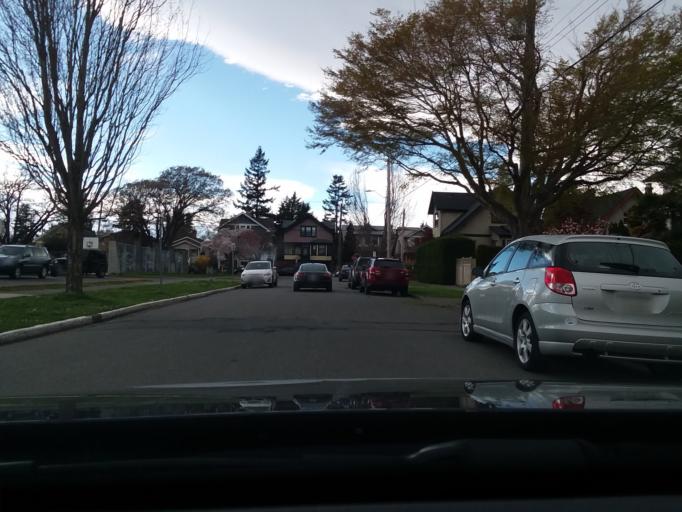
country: CA
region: British Columbia
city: Victoria
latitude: 48.4162
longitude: -123.3475
